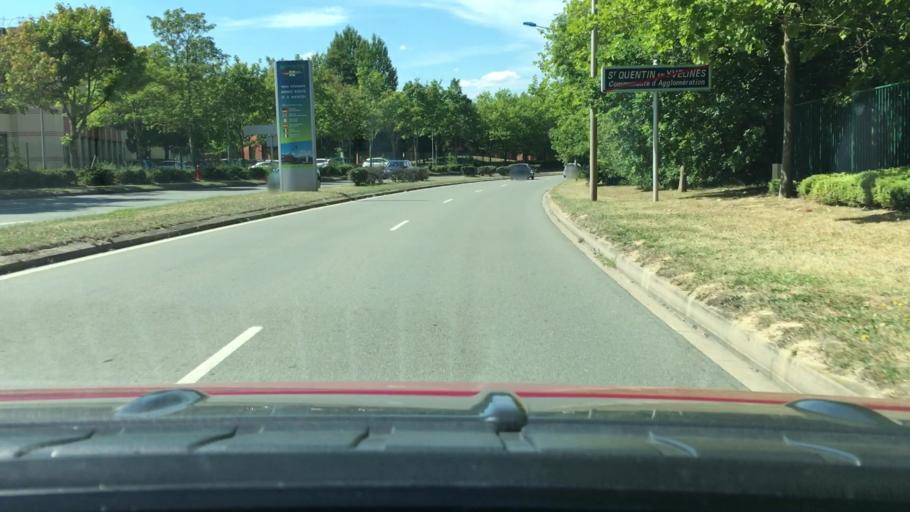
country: FR
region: Ile-de-France
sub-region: Departement des Yvelines
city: Bois-d'Arcy
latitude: 48.7939
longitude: 2.0352
